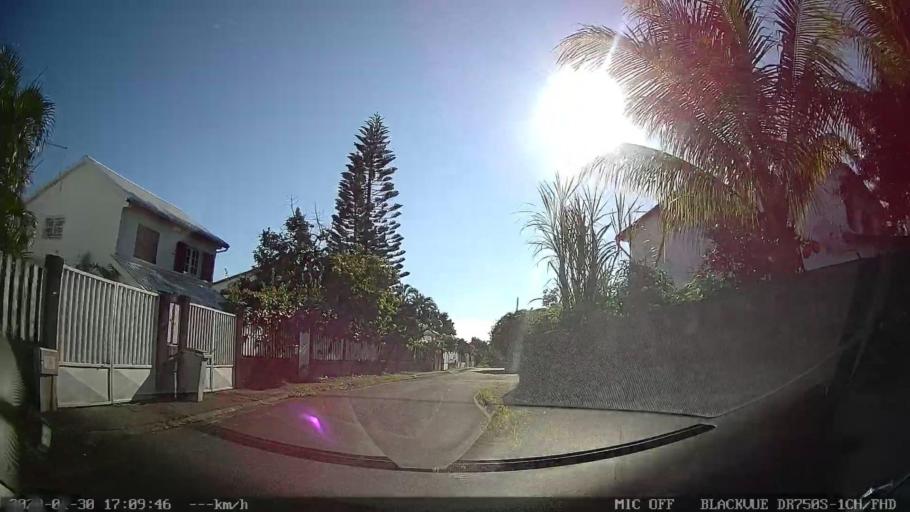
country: RE
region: Reunion
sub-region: Reunion
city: Sainte-Marie
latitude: -20.9139
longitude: 55.5124
